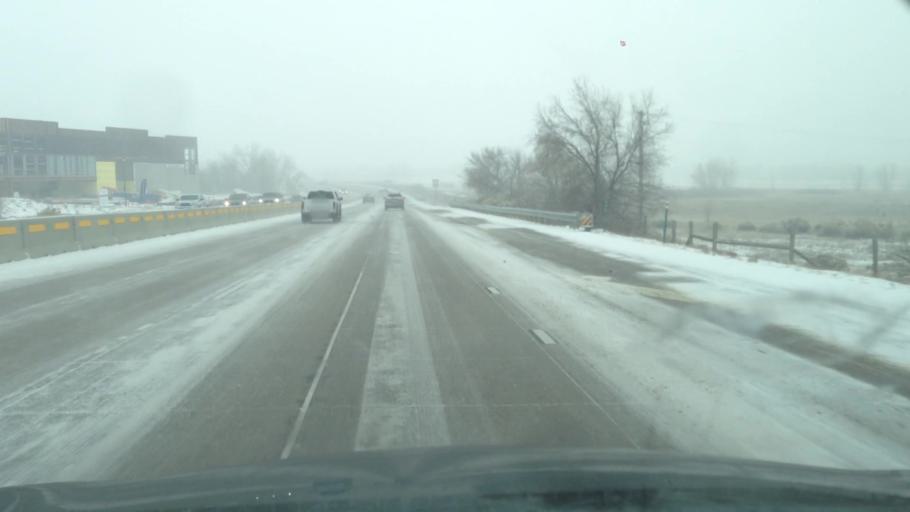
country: US
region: Colorado
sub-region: Arapahoe County
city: Dove Valley
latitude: 39.6214
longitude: -104.8208
